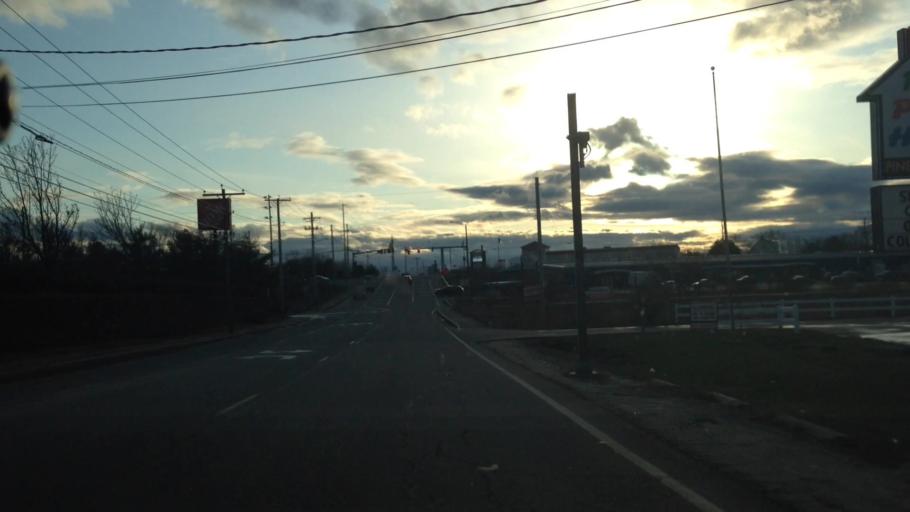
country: US
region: Maine
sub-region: Cumberland County
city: Westbrook
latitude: 43.6865
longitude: -70.3253
